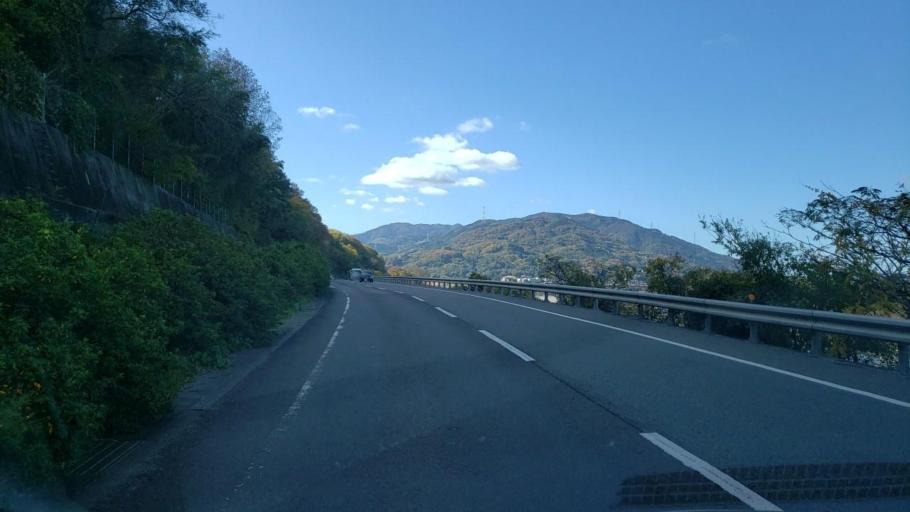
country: JP
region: Tokushima
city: Wakimachi
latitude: 34.0615
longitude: 134.1877
